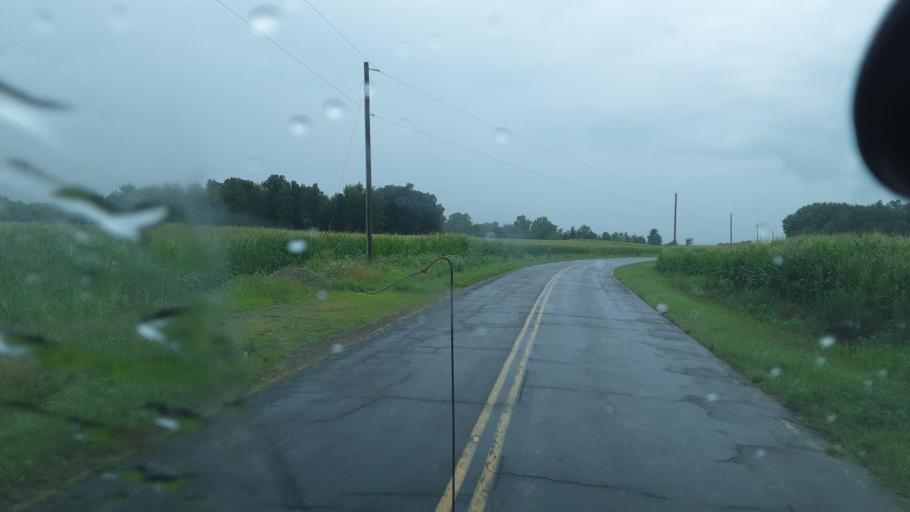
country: US
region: Ohio
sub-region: Williams County
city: Edgerton
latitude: 41.4971
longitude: -84.7909
